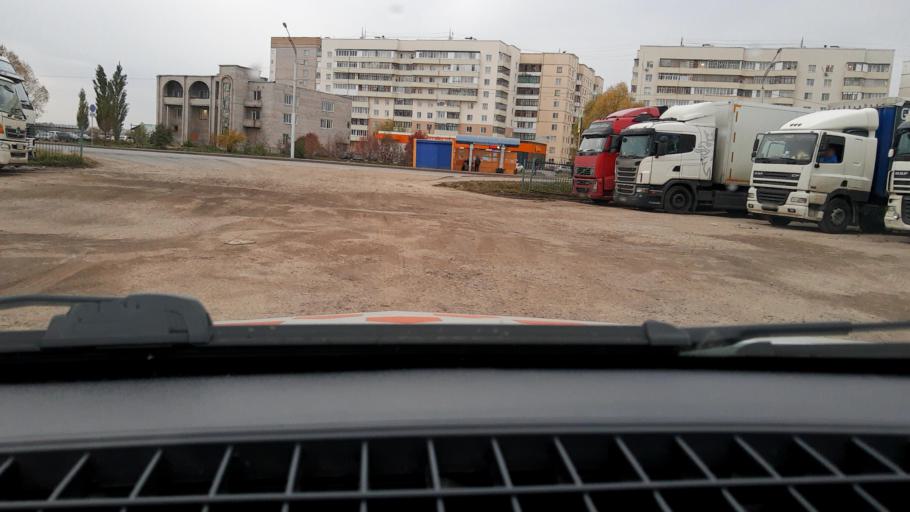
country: RU
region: Bashkortostan
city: Iglino
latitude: 54.7560
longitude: 56.2501
